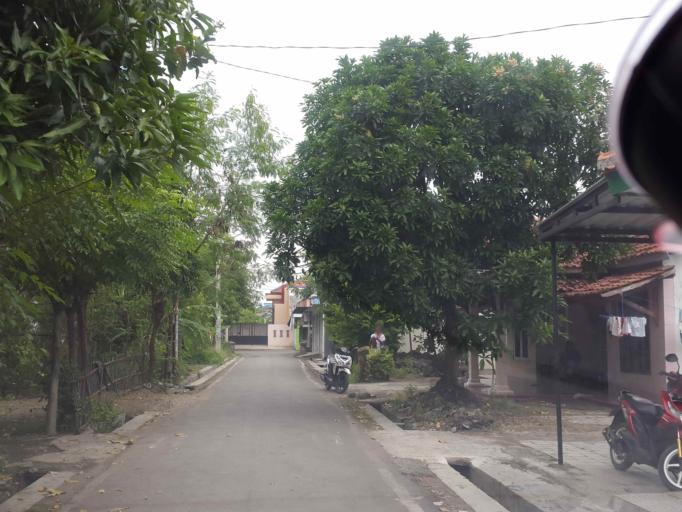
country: ID
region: Central Java
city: Dukuhturi
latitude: -6.8831
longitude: 109.1035
